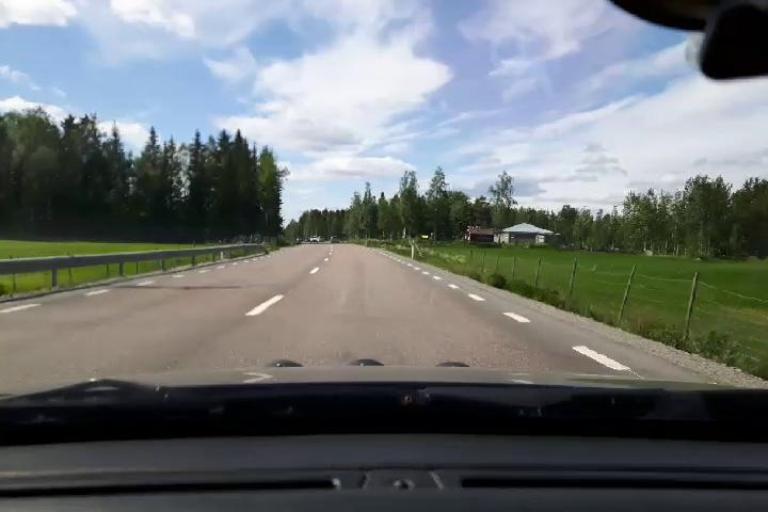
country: SE
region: Gaevleborg
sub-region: Bollnas Kommun
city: Bollnas
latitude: 61.3068
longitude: 16.4609
